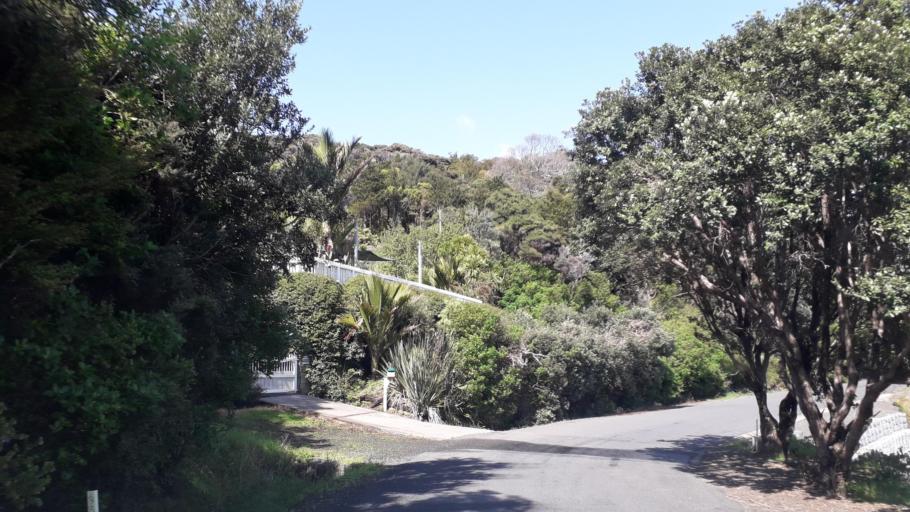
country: NZ
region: Northland
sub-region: Far North District
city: Paihia
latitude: -35.2279
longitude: 174.2635
